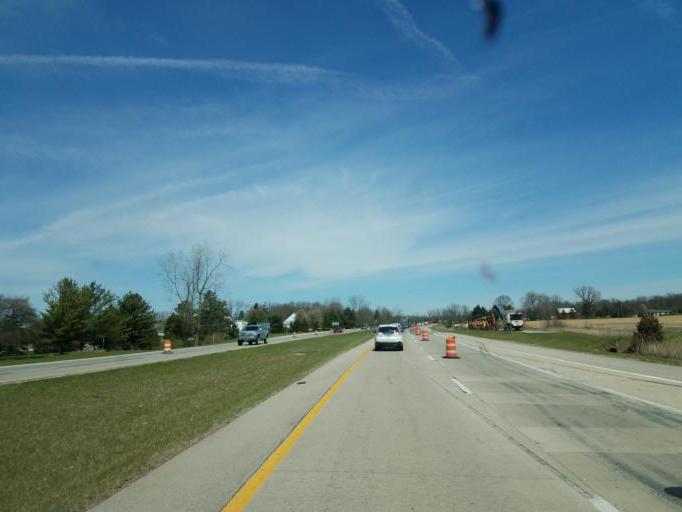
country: US
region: Ohio
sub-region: Marion County
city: Prospect
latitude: 40.4272
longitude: -83.0741
